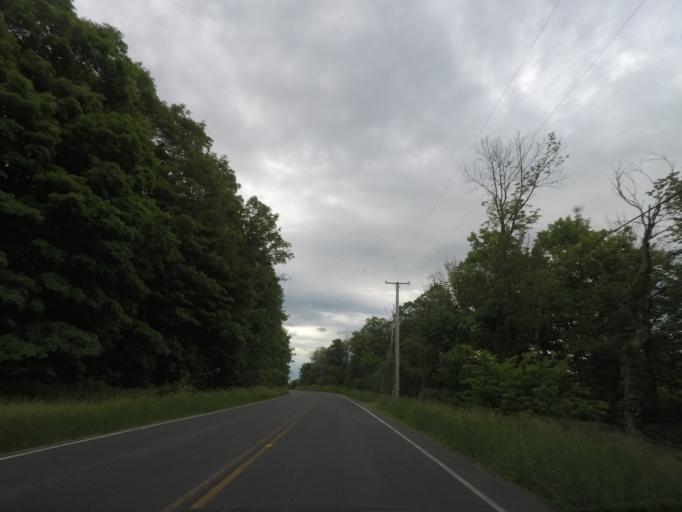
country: US
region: New York
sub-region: Dutchess County
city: Pine Plains
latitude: 41.9681
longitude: -73.5546
